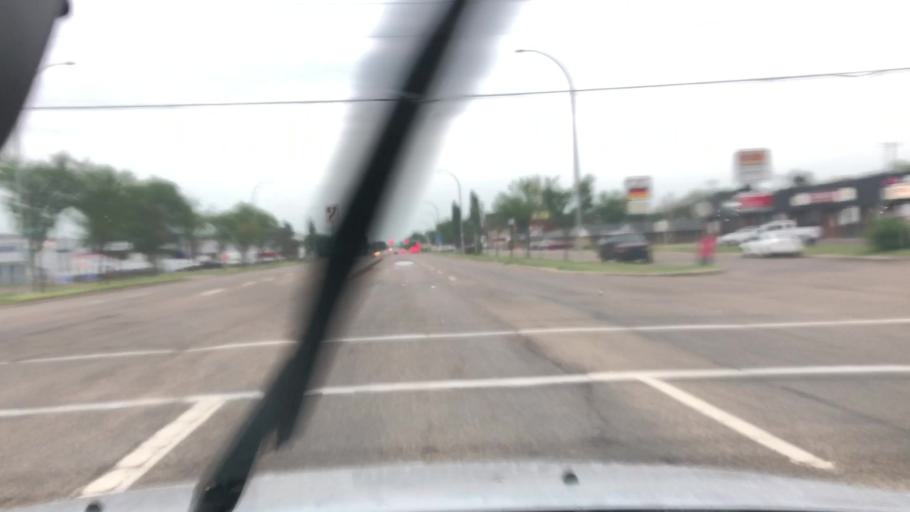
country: CA
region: Alberta
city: St. Albert
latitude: 53.5589
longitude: -113.5844
